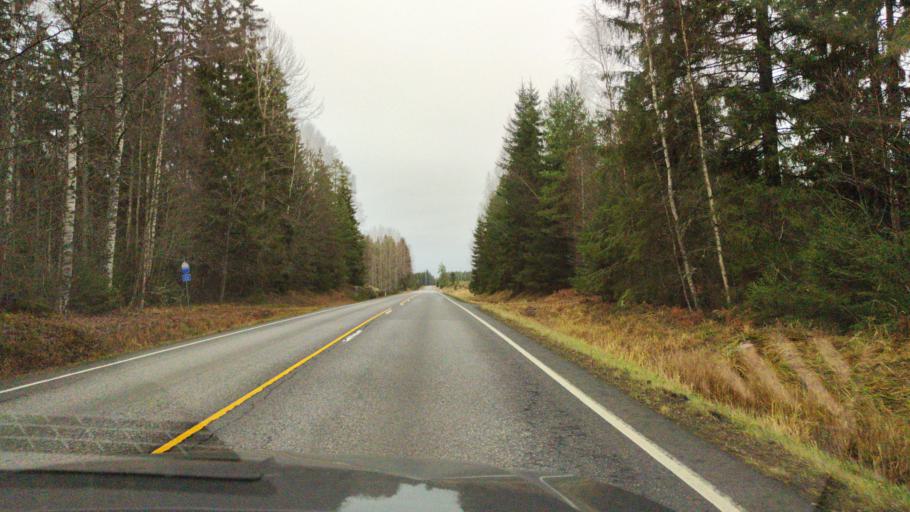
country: FI
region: Varsinais-Suomi
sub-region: Loimaa
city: Ylaene
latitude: 60.7558
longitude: 22.4288
